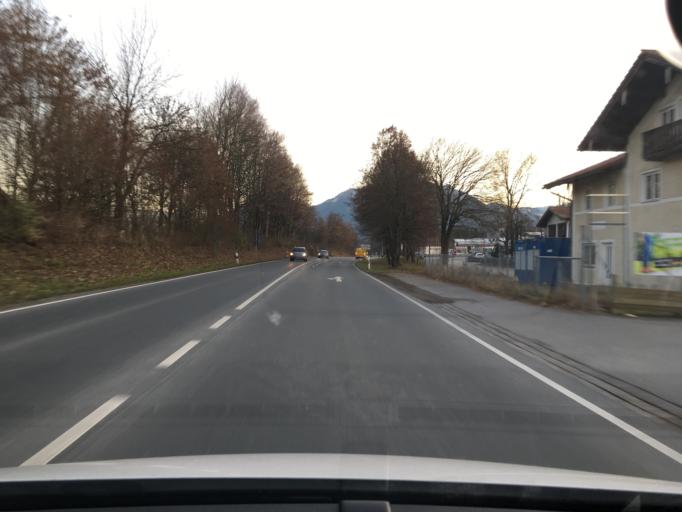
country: DE
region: Bavaria
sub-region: Upper Bavaria
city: Raubling
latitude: 47.7682
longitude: 12.1064
